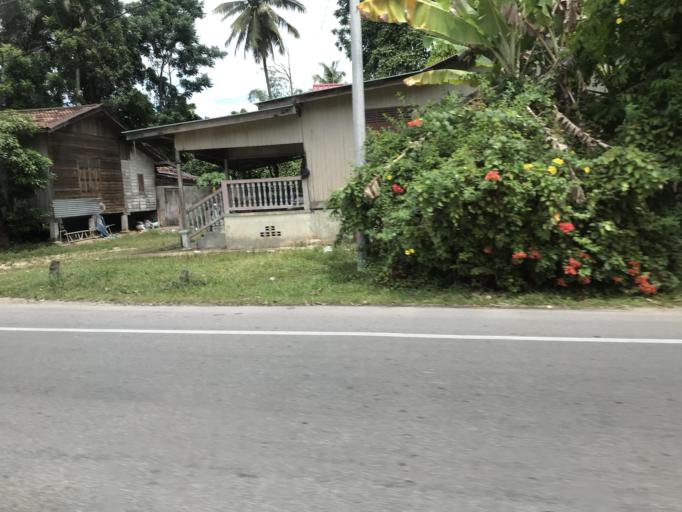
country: MY
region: Kelantan
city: Tumpat
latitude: 6.1699
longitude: 102.1903
